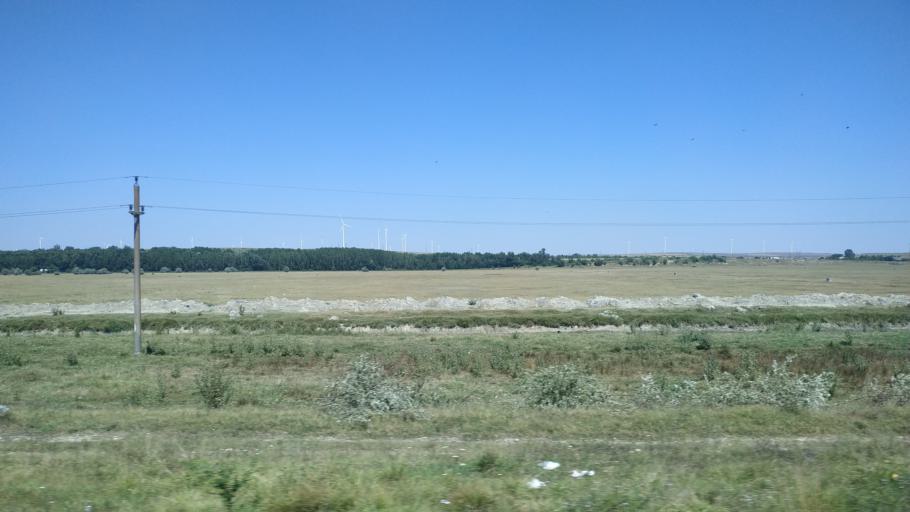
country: RO
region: Constanta
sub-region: Comuna Mircea Voda
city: Mircea Voda
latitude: 44.2644
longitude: 28.1628
